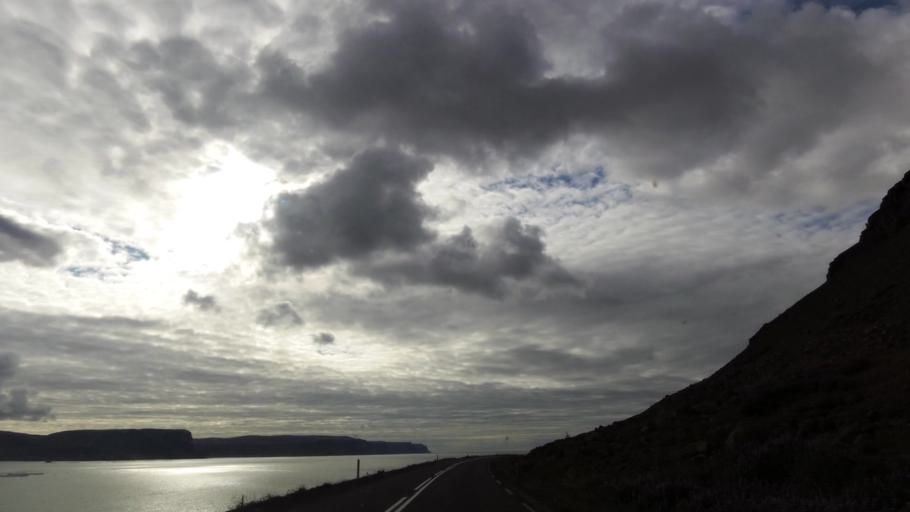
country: IS
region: West
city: Olafsvik
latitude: 65.5817
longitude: -23.9586
